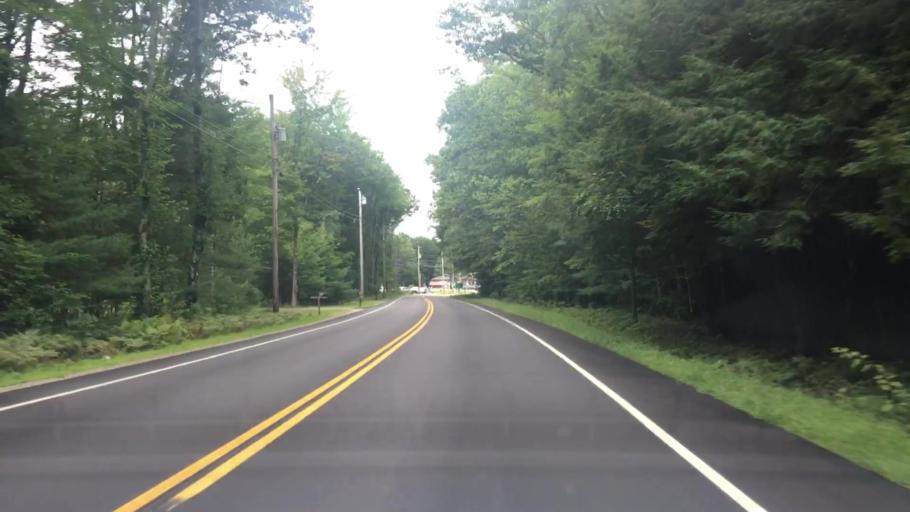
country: US
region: Maine
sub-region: York County
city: West Kennebunk
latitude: 43.4769
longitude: -70.6039
